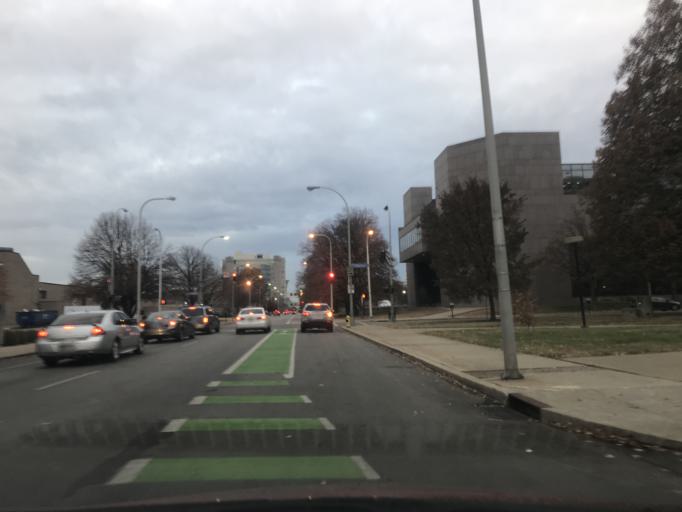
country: US
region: Kentucky
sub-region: Jefferson County
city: Louisville
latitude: 38.2491
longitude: -85.7629
